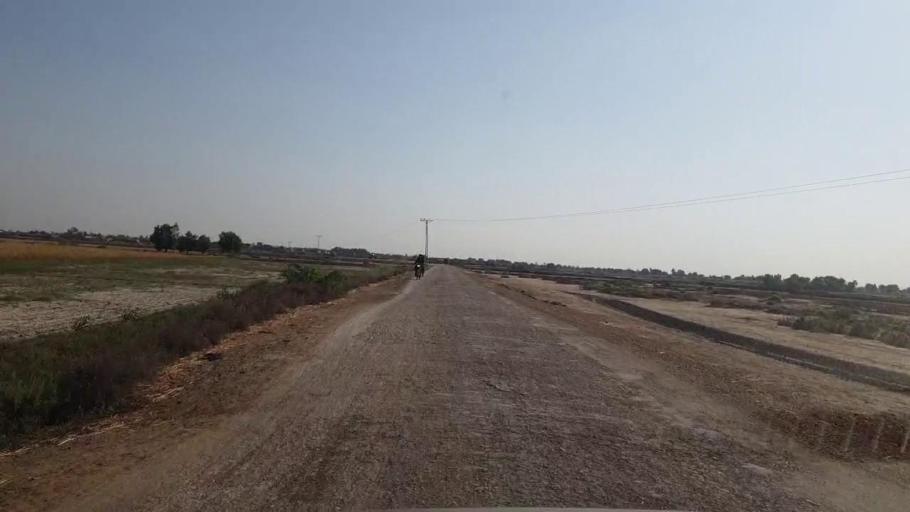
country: PK
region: Sindh
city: Matli
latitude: 25.0445
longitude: 68.7231
